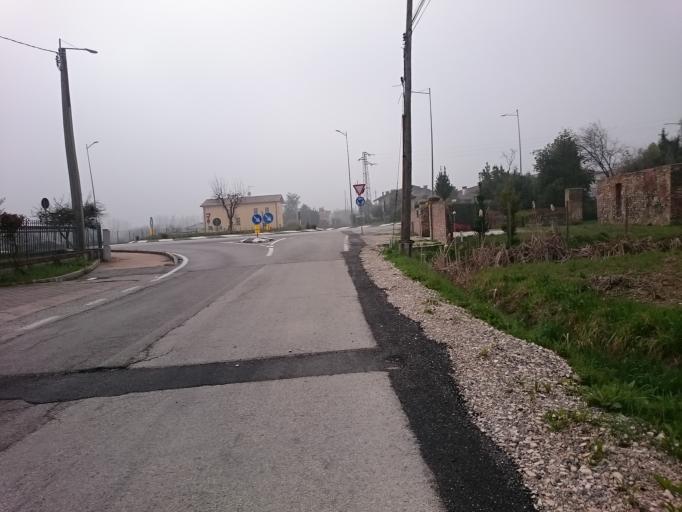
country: IT
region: Veneto
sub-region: Provincia di Padova
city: Due Carrare
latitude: 45.2967
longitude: 11.8384
